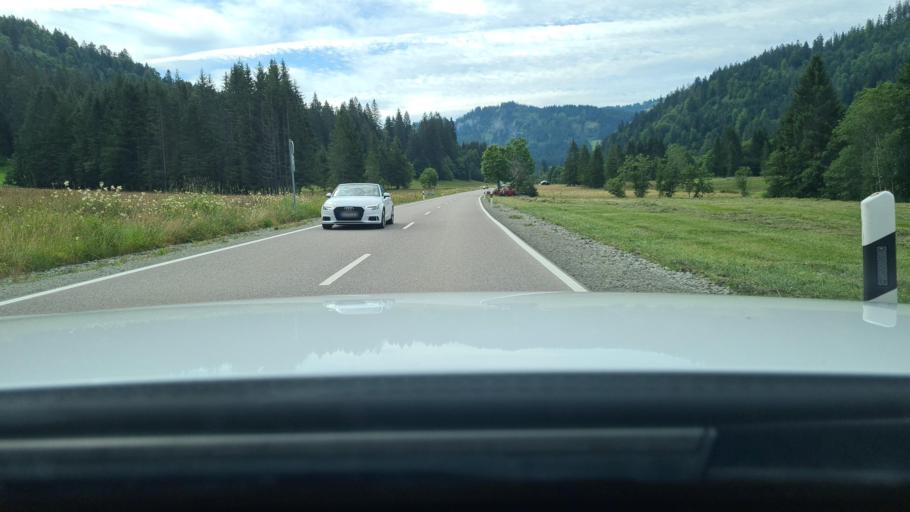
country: DE
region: Bavaria
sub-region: Swabia
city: Balderschwang
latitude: 47.4544
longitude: 10.1317
